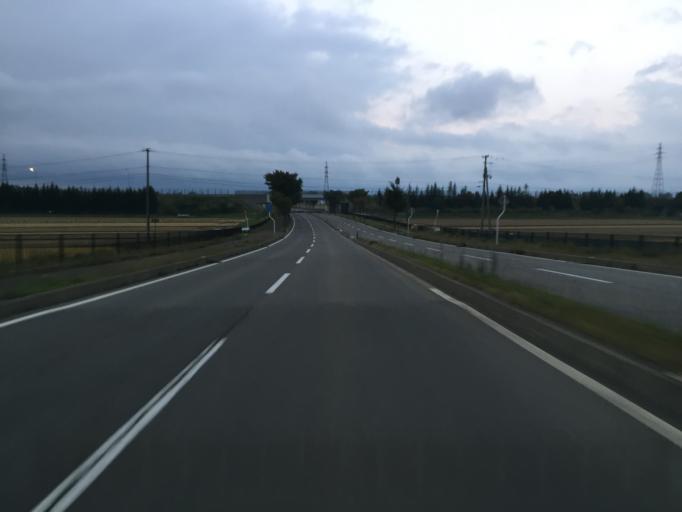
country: JP
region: Fukushima
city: Inawashiro
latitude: 37.5444
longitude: 140.1106
